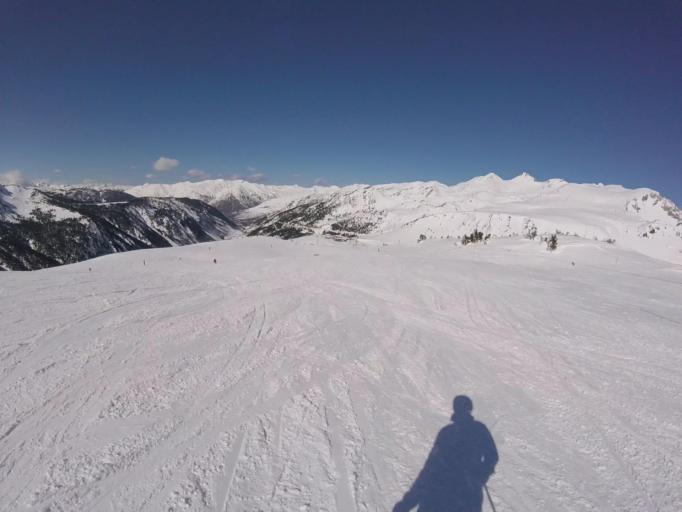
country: ES
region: Catalonia
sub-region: Provincia de Lleida
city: Espot
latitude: 42.6550
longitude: 0.9833
